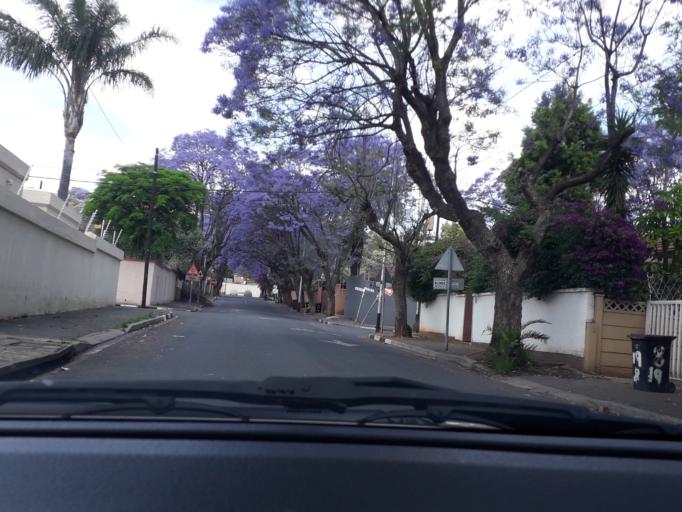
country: ZA
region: Gauteng
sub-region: City of Johannesburg Metropolitan Municipality
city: Johannesburg
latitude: -26.1626
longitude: 28.0865
